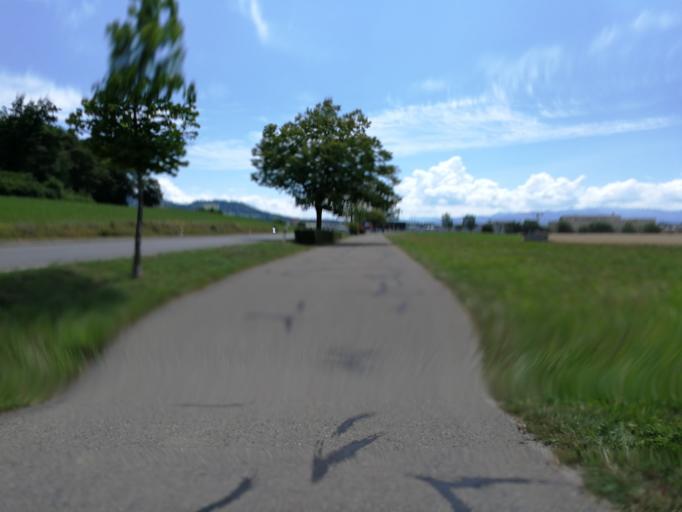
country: CH
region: Zurich
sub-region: Bezirk Hinwil
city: Hinwil
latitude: 47.3086
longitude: 8.8302
